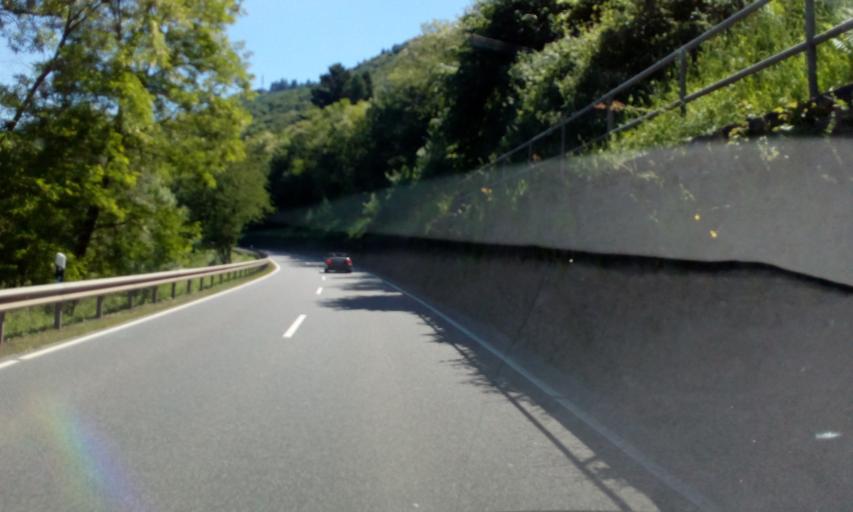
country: DE
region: Rheinland-Pfalz
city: Monzelfeld
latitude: 49.9061
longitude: 7.0532
